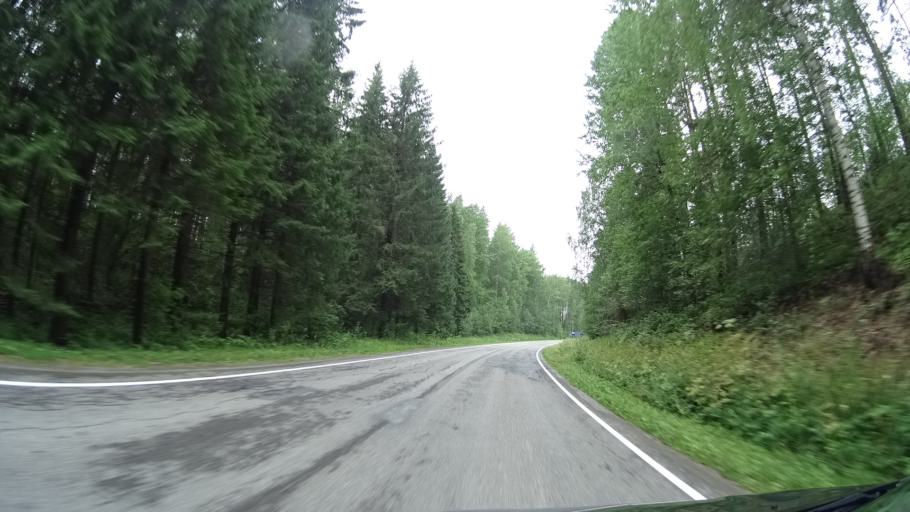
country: FI
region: Southern Savonia
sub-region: Savonlinna
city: Punkaharju
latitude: 61.7514
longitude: 29.4391
